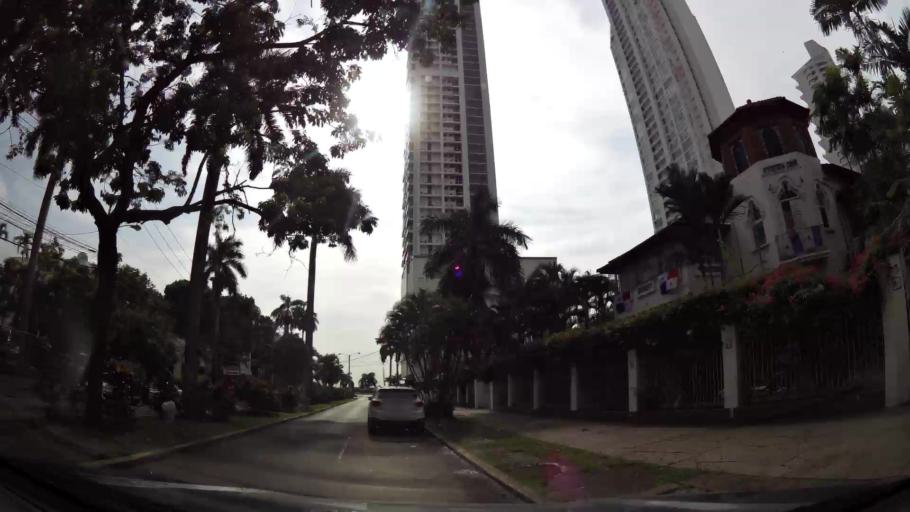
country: PA
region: Panama
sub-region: Distrito de Panama
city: Ancon
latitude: 8.9684
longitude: -79.5339
